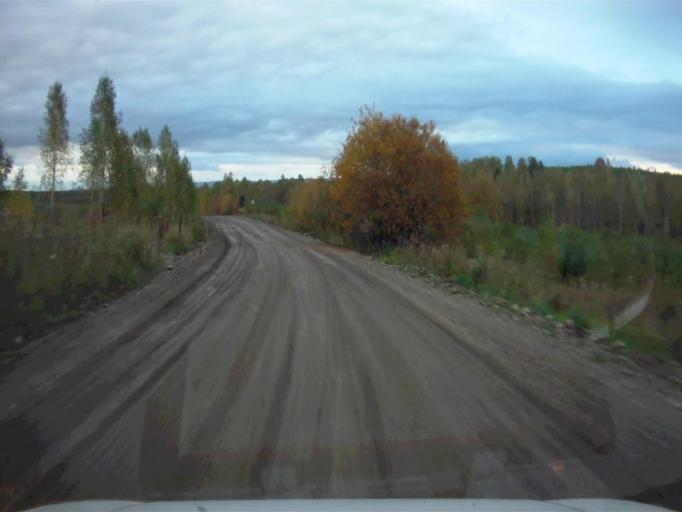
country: RU
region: Sverdlovsk
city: Mikhaylovsk
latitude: 56.2091
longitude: 59.2098
